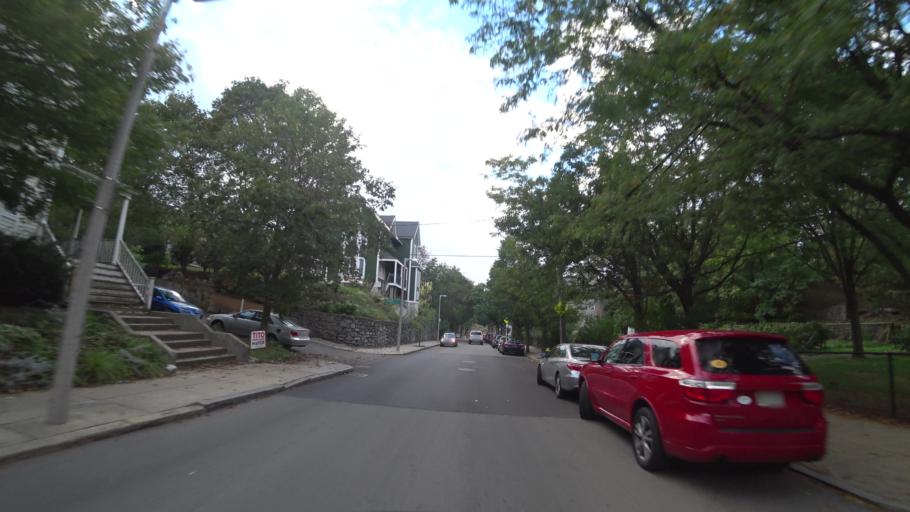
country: US
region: Massachusetts
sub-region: Norfolk County
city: Brookline
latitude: 42.3270
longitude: -71.0933
